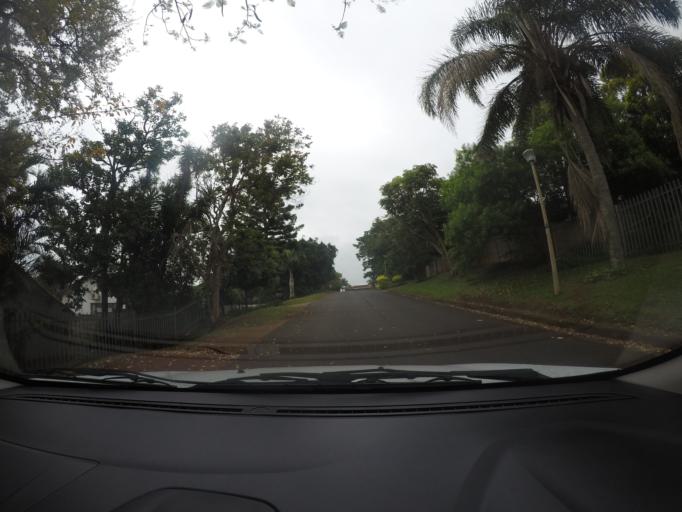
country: ZA
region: KwaZulu-Natal
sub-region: uThungulu District Municipality
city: Empangeni
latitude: -28.7560
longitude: 31.8849
